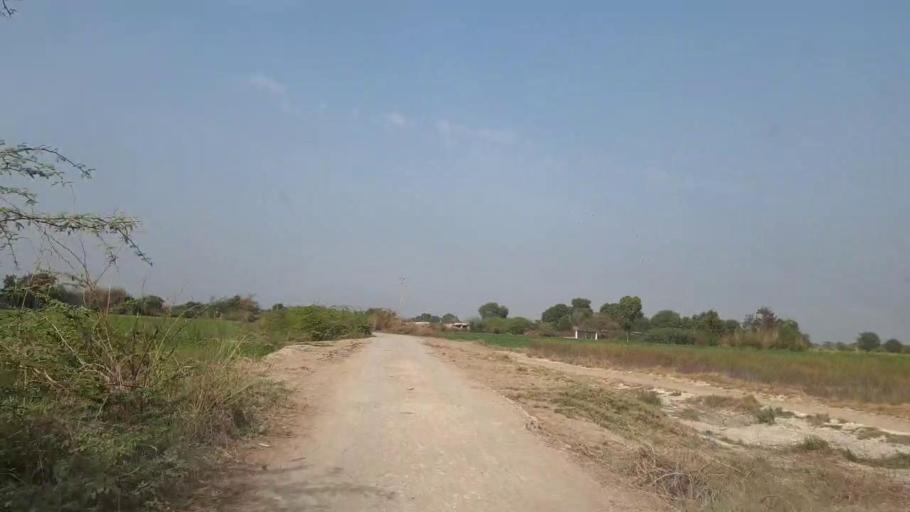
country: PK
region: Sindh
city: Mirpur Khas
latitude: 25.5698
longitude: 69.1522
